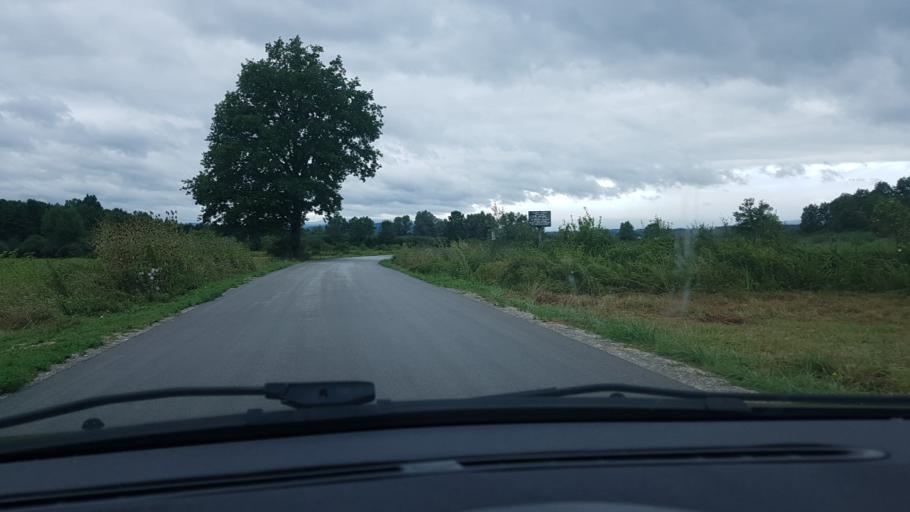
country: HR
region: Karlovacka
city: Ozalj
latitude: 45.5825
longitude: 15.5388
